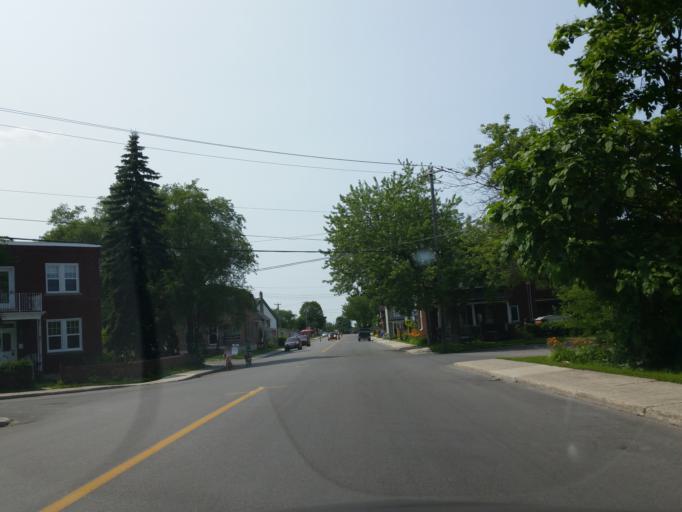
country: CA
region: Ontario
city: Bells Corners
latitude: 45.3961
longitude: -75.8452
